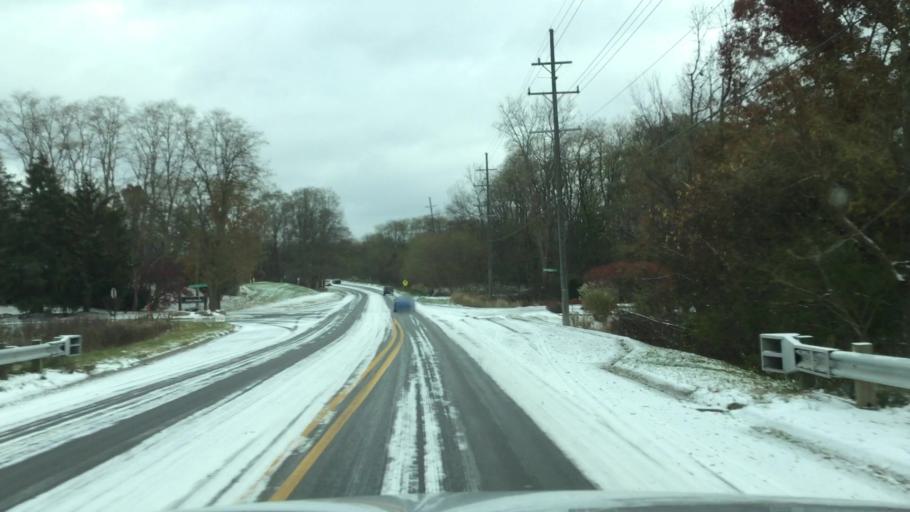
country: US
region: Michigan
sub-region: Livingston County
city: Brighton
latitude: 42.5287
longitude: -83.8185
